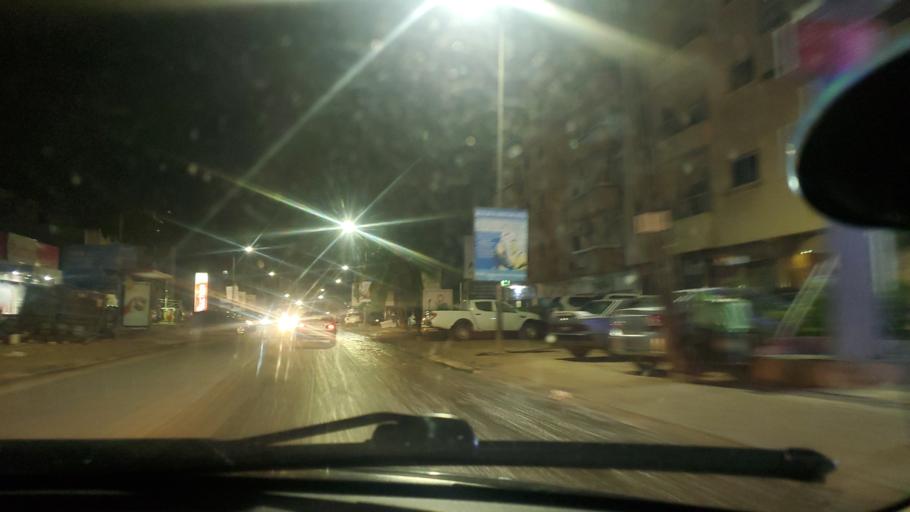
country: SN
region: Dakar
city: Grand Dakar
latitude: 14.7231
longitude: -17.4463
